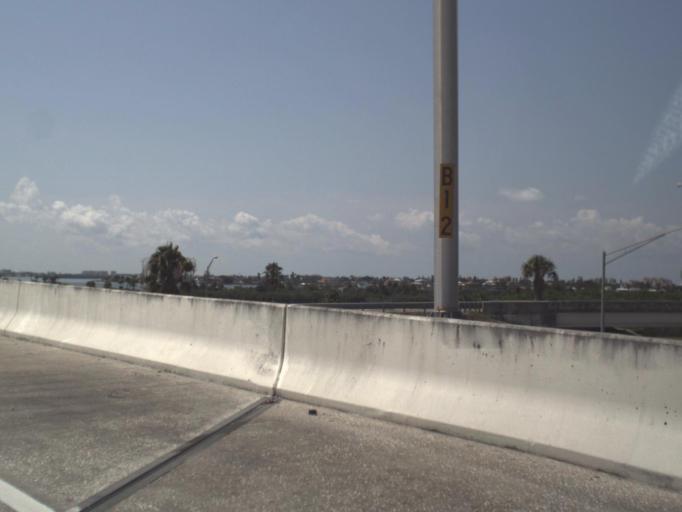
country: US
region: Florida
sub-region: Pinellas County
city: Bay Pines
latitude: 27.8151
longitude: -82.7862
